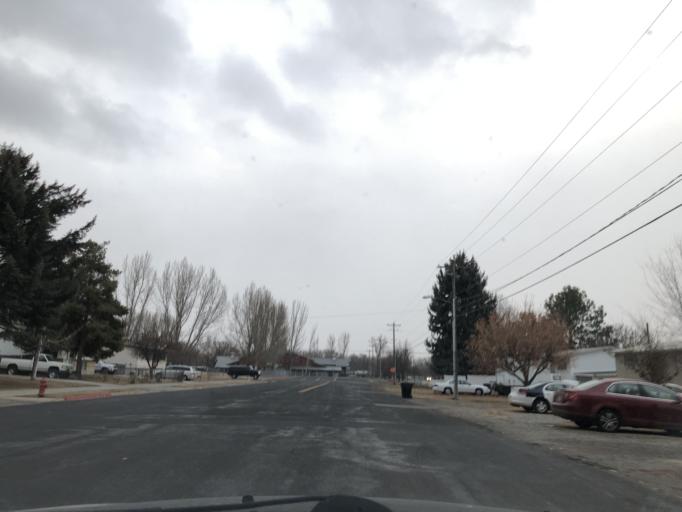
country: US
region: Utah
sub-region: Cache County
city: Logan
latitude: 41.7253
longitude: -111.8481
